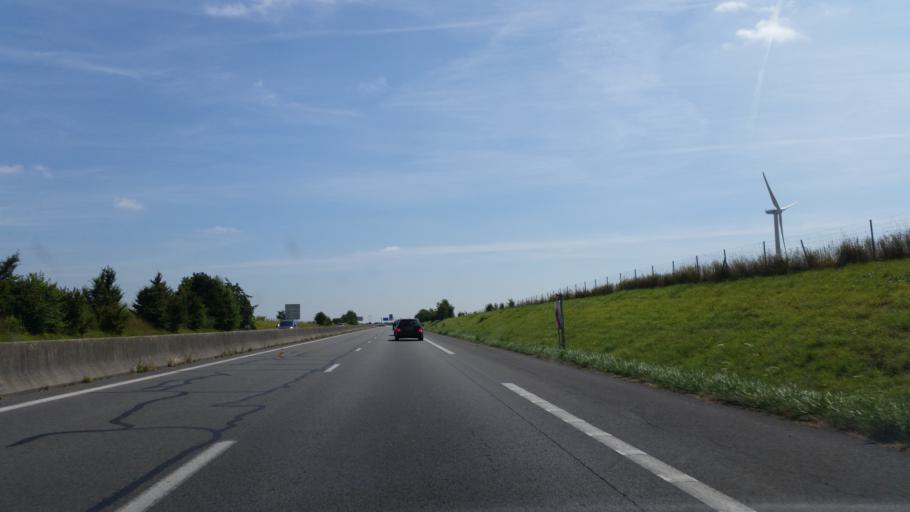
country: FR
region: Picardie
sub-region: Departement de la Somme
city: Chaulnes
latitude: 49.8543
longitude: 2.7966
